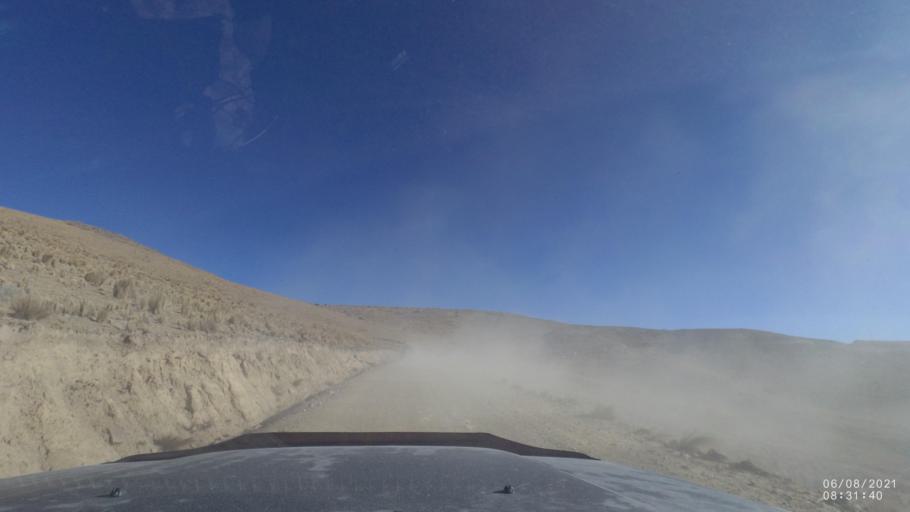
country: BO
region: Cochabamba
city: Sipe Sipe
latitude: -17.1849
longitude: -66.3733
